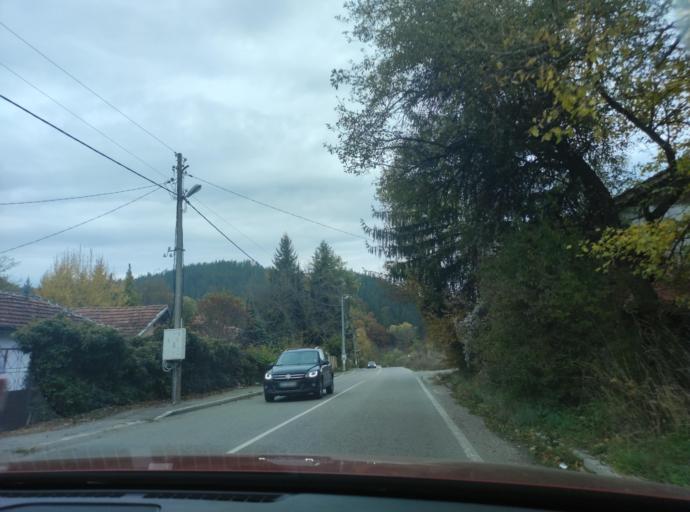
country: BG
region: Sofiya
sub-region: Obshtina Godech
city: Godech
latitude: 42.9735
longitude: 23.1399
